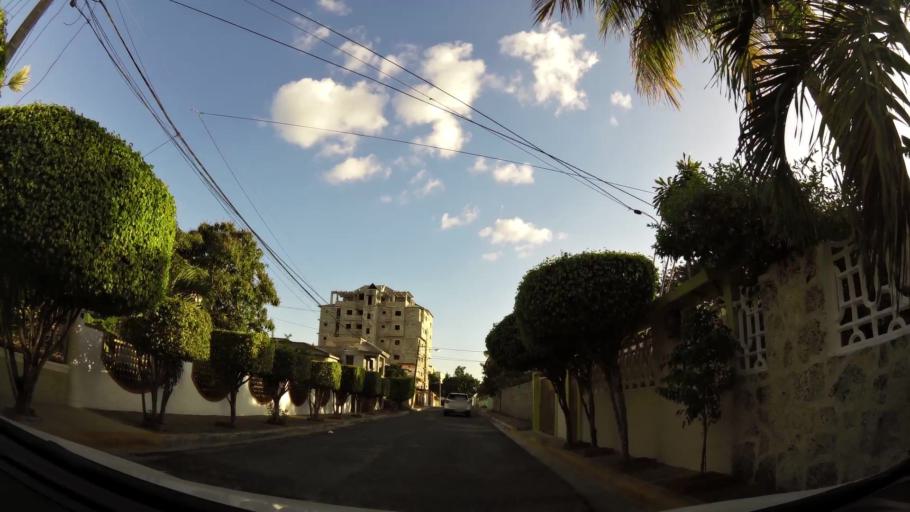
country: DO
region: Santo Domingo
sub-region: Santo Domingo
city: Santo Domingo Este
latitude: 18.4787
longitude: -69.8302
